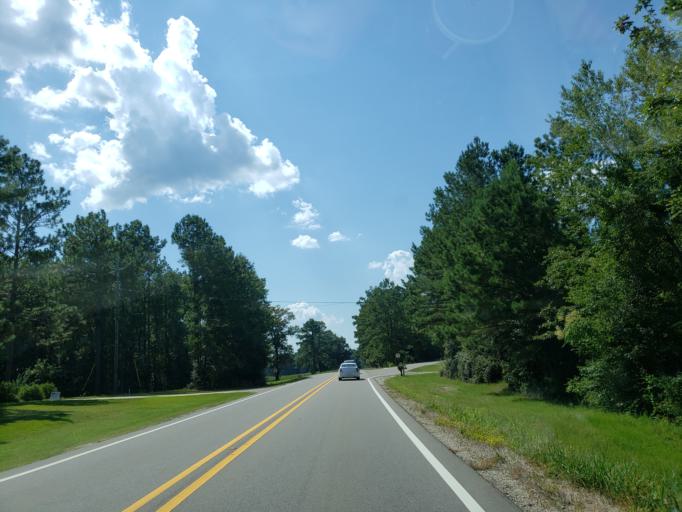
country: US
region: Mississippi
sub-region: Lamar County
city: Sumrall
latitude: 31.3878
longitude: -89.5343
